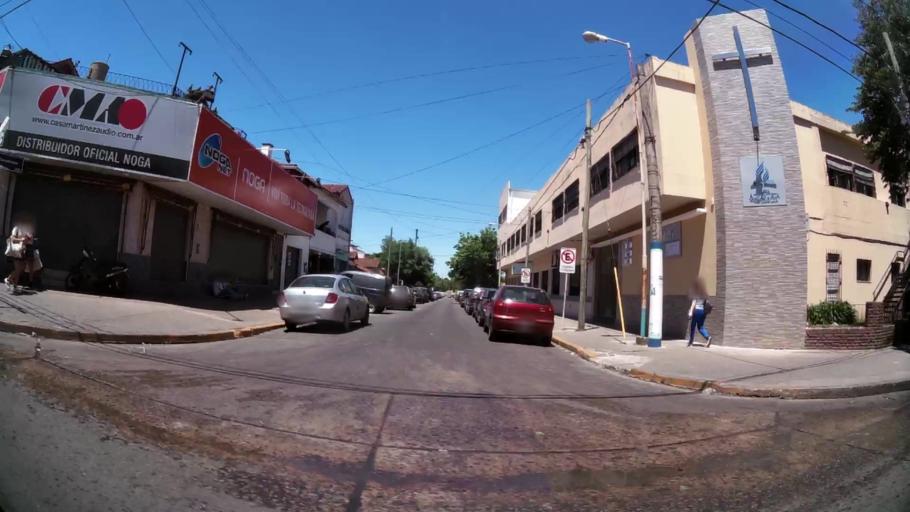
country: AR
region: Buenos Aires
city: Hurlingham
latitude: -34.5010
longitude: -58.6932
